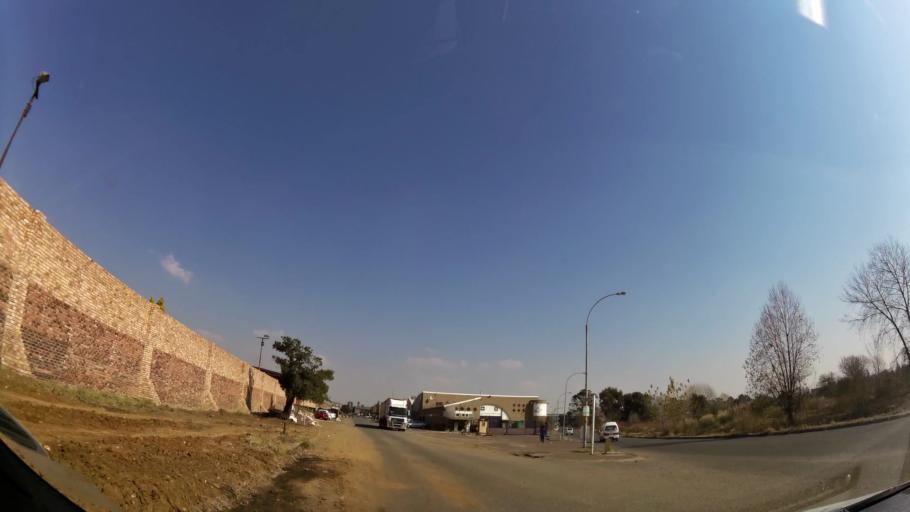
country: ZA
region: Gauteng
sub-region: Ekurhuleni Metropolitan Municipality
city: Benoni
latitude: -26.2008
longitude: 28.3093
